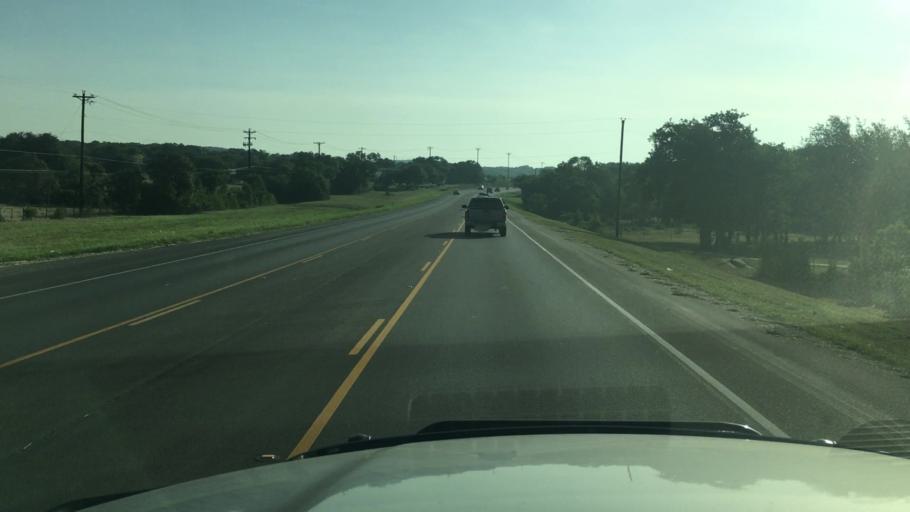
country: US
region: Texas
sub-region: Hays County
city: Dripping Springs
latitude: 30.2022
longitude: -98.1533
